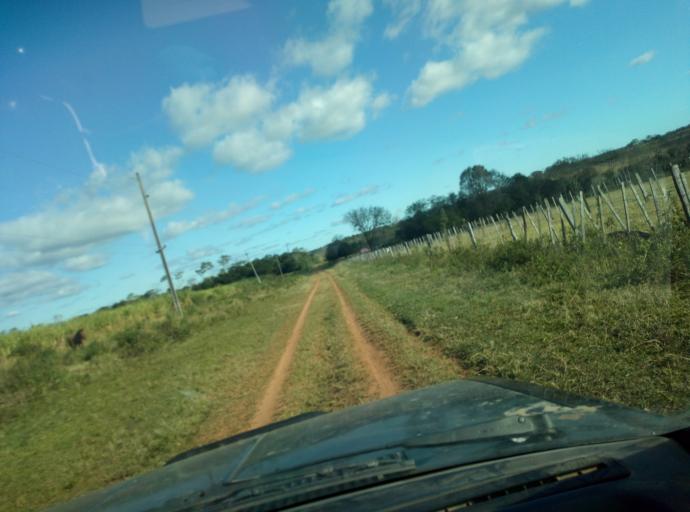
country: PY
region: Caaguazu
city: Doctor Cecilio Baez
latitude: -25.1662
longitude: -56.2726
